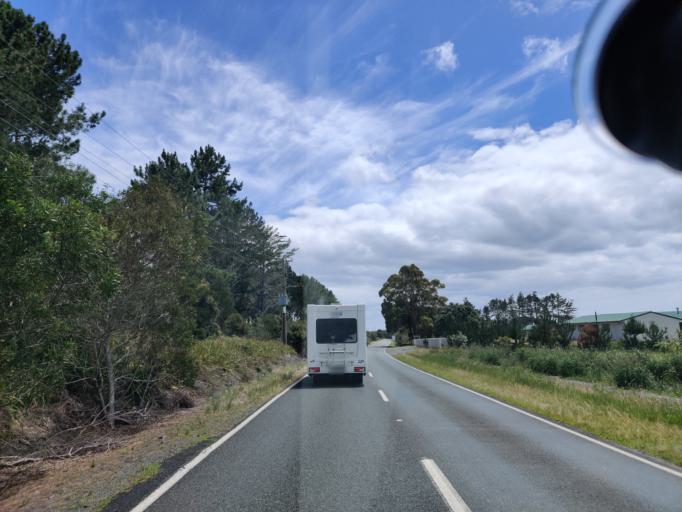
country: NZ
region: Northland
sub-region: Far North District
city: Kaitaia
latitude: -34.7438
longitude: 173.0471
